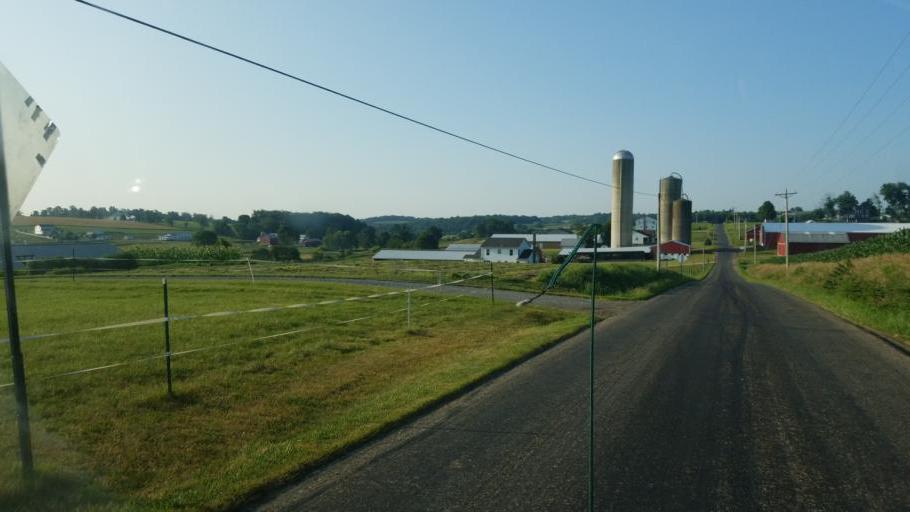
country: US
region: Ohio
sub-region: Wayne County
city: Dalton
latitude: 40.6728
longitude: -81.7308
